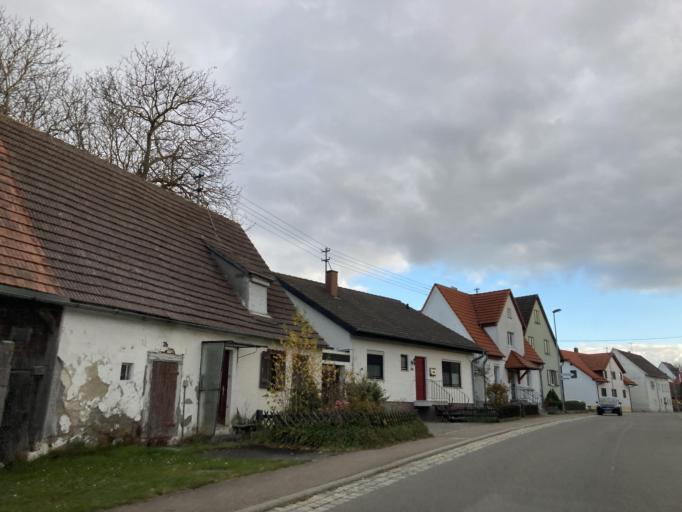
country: DE
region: Baden-Wuerttemberg
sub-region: Tuebingen Region
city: Haigerloch
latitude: 48.4335
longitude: 8.7828
